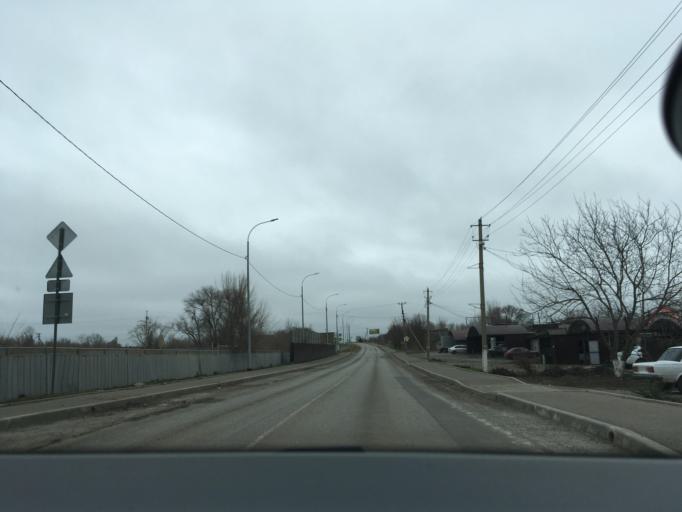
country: RU
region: Krasnodarskiy
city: Kushchevskaya
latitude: 46.5774
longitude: 39.6364
